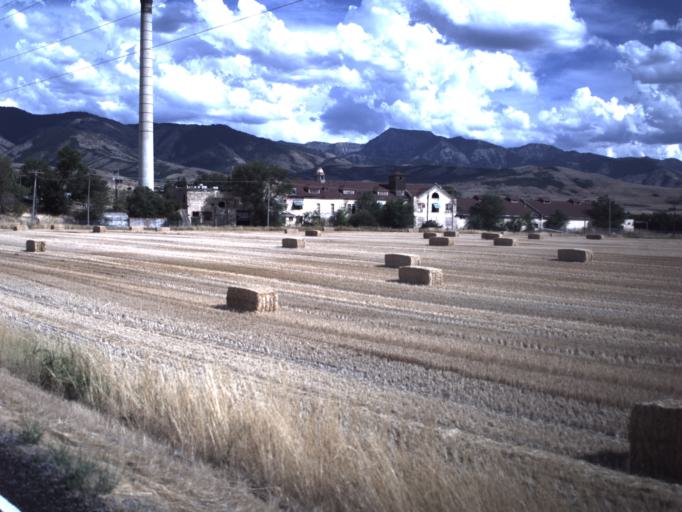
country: US
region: Utah
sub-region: Cache County
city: Richmond
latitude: 41.9229
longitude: -111.8261
